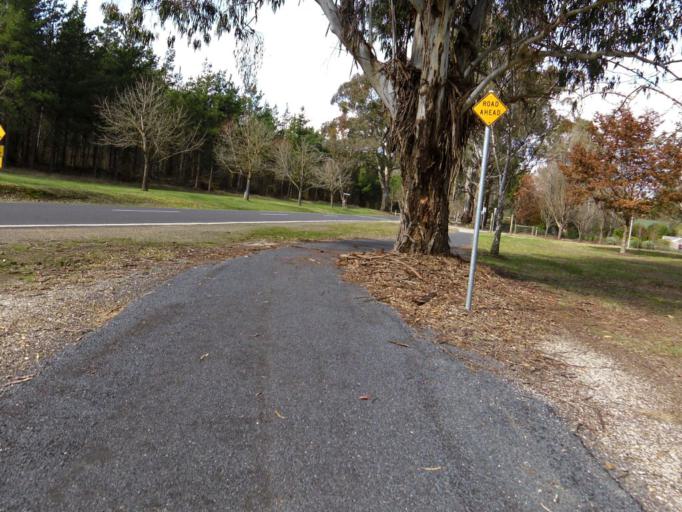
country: AU
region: Victoria
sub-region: Alpine
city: Mount Beauty
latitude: -36.7142
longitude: 146.9406
